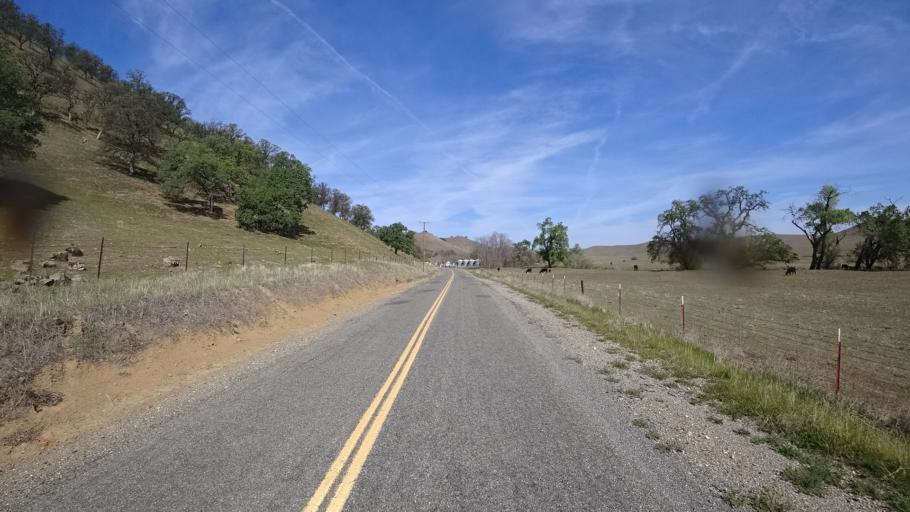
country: US
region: California
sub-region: Glenn County
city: Willows
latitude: 39.5450
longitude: -122.3977
